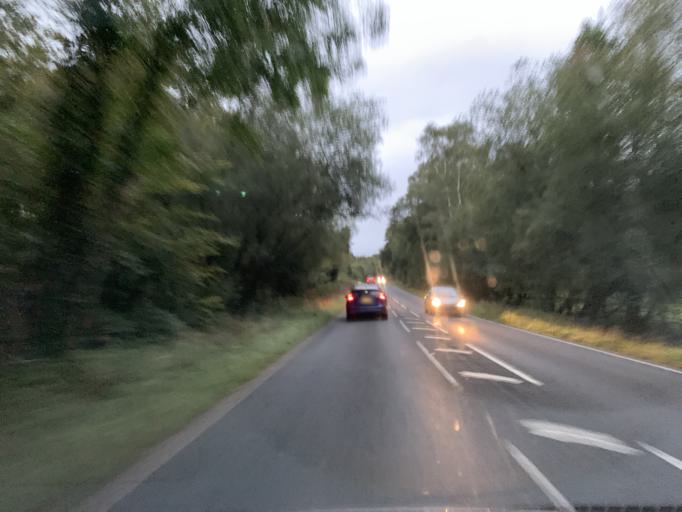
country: GB
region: England
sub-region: Hampshire
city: Cadnam
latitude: 50.9143
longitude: -1.5821
